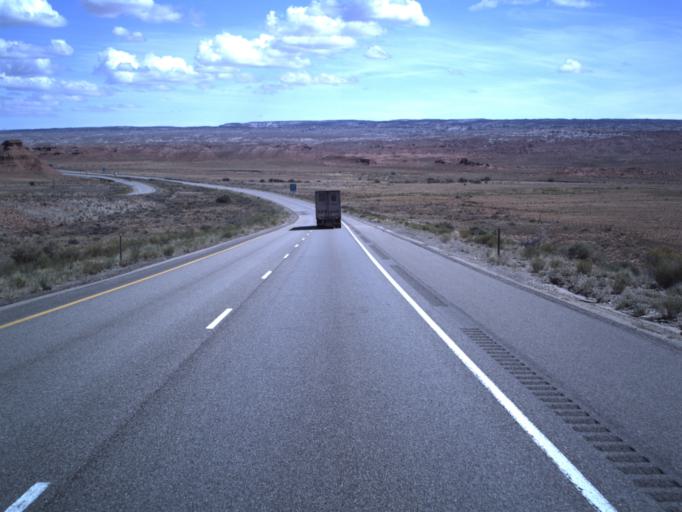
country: US
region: Utah
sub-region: Emery County
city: Ferron
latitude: 38.8388
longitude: -111.0822
